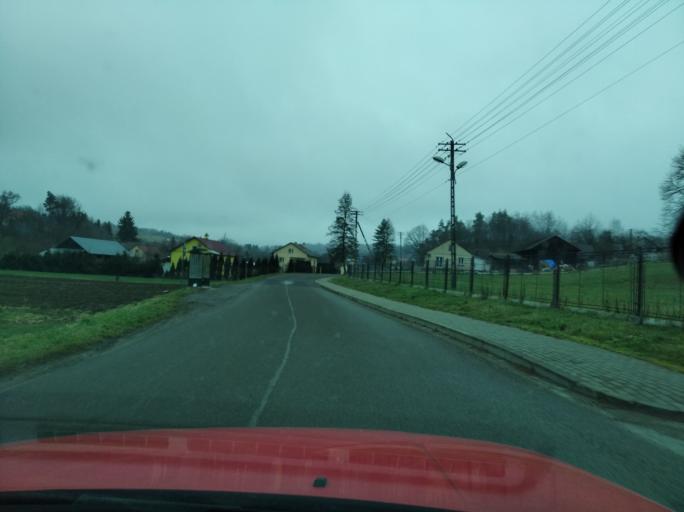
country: PL
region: Subcarpathian Voivodeship
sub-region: Powiat przemyski
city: Nienadowa
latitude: 49.8373
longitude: 22.4337
